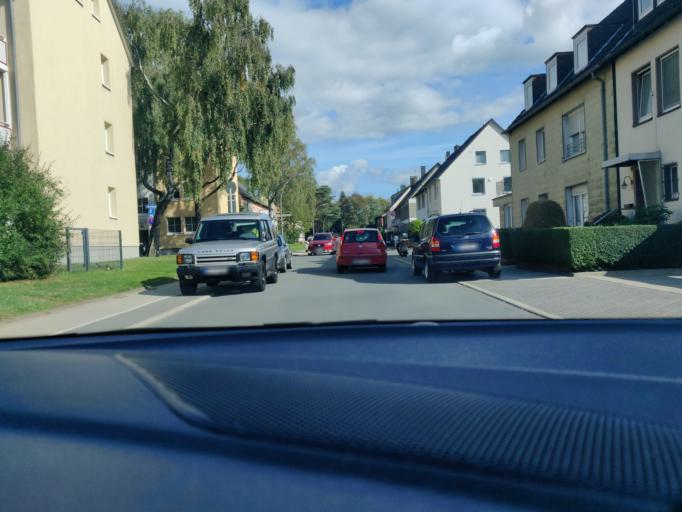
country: DE
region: North Rhine-Westphalia
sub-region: Regierungsbezirk Dusseldorf
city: Velbert
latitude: 51.3299
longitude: 7.0297
